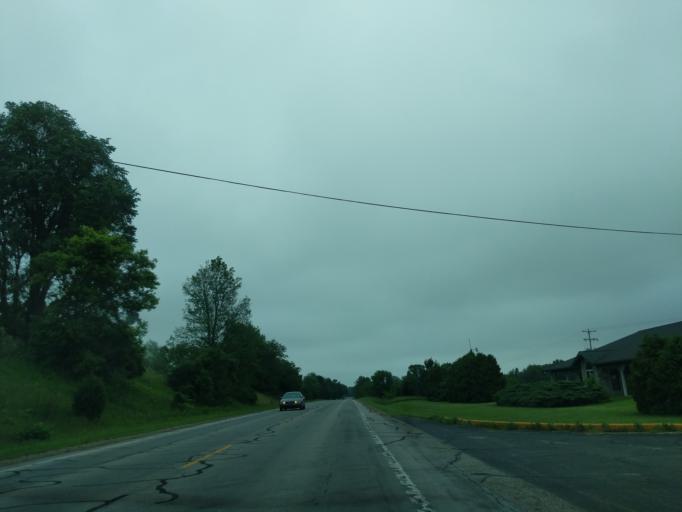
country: US
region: Michigan
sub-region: Hillsdale County
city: Litchfield
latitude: 42.0645
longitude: -84.7850
